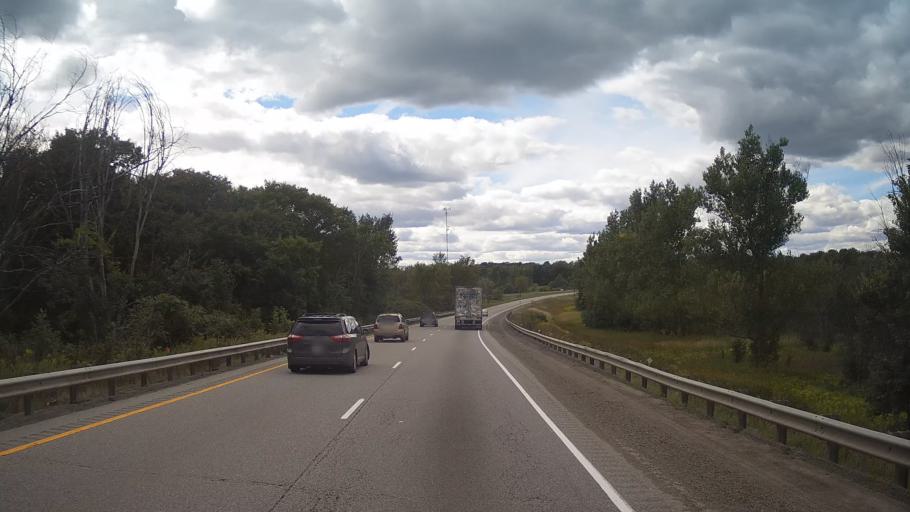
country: CA
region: Ontario
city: Brockville
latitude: 44.5196
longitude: -75.7894
